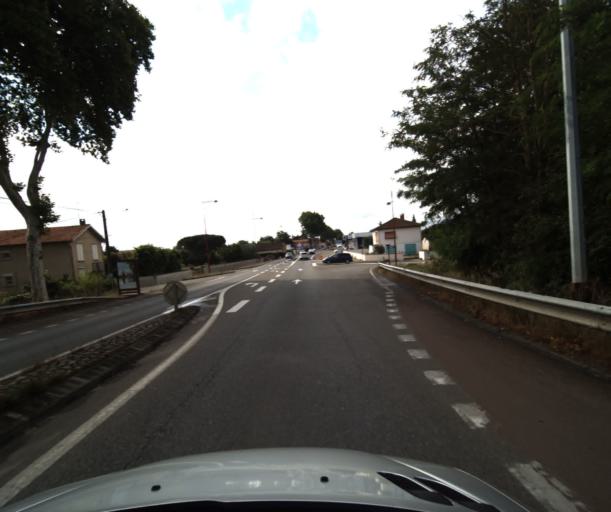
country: FR
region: Midi-Pyrenees
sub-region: Departement du Tarn-et-Garonne
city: Castelsarrasin
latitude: 44.0529
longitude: 1.1008
